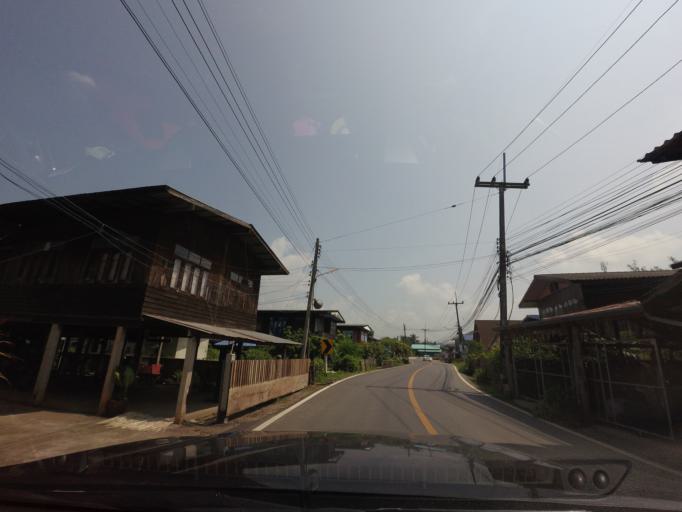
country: TH
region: Nan
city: Nan
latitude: 18.8592
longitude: 100.8185
